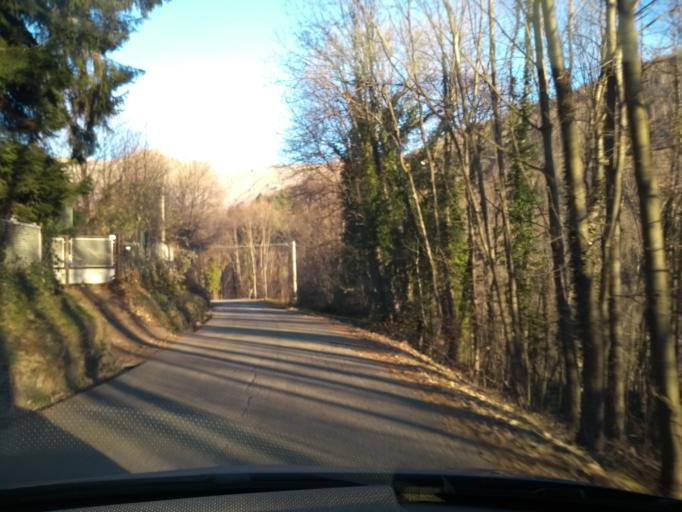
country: IT
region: Piedmont
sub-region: Provincia di Torino
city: Corio
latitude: 45.3189
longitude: 7.5296
